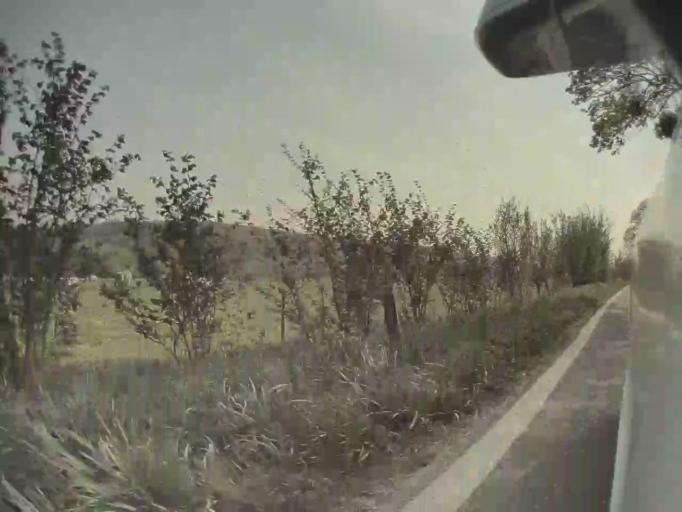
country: BE
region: Wallonia
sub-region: Province de Namur
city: Havelange
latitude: 50.3337
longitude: 5.2795
